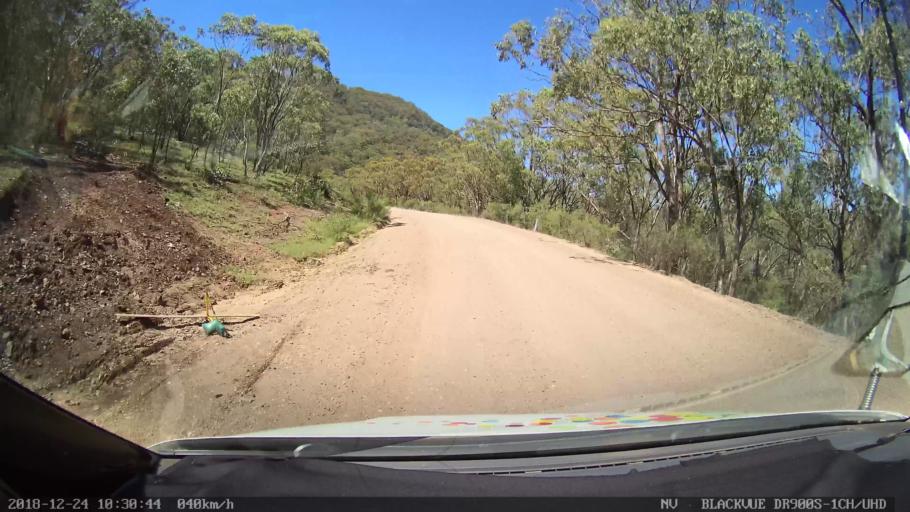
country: AU
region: New South Wales
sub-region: Upper Hunter Shire
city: Merriwa
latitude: -31.8361
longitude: 150.5237
